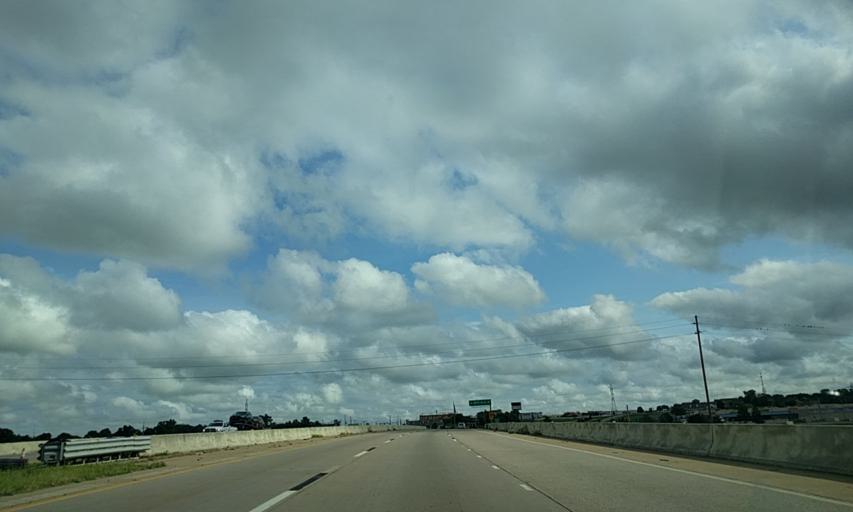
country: US
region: Oklahoma
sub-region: Tulsa County
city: Owasso
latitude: 36.2772
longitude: -95.8479
